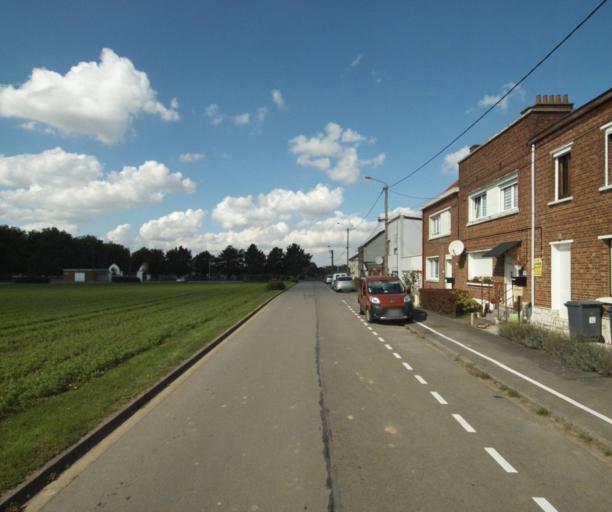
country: FR
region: Nord-Pas-de-Calais
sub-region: Departement du Nord
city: Illies
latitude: 50.5616
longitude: 2.8384
